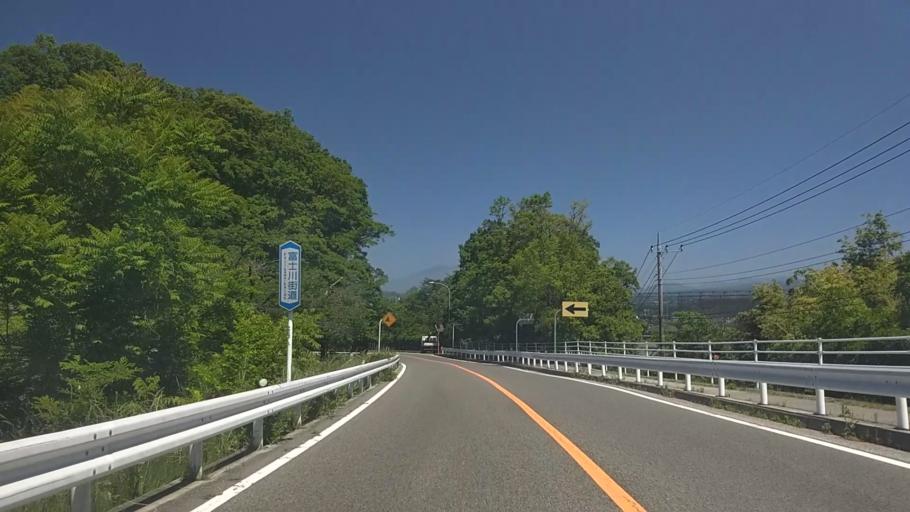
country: JP
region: Yamanashi
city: Nirasaki
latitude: 35.6843
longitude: 138.4628
